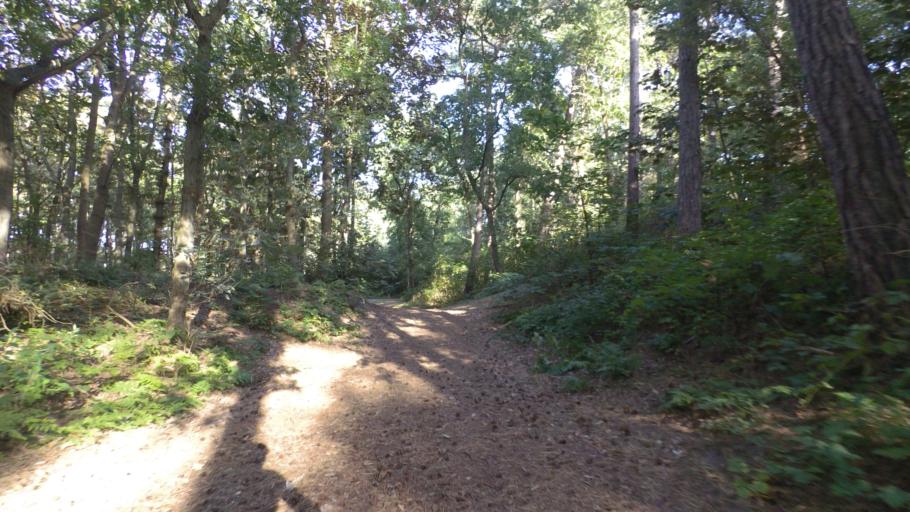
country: NL
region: Friesland
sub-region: Gemeente Ameland
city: Nes
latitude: 53.4556
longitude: 5.7815
